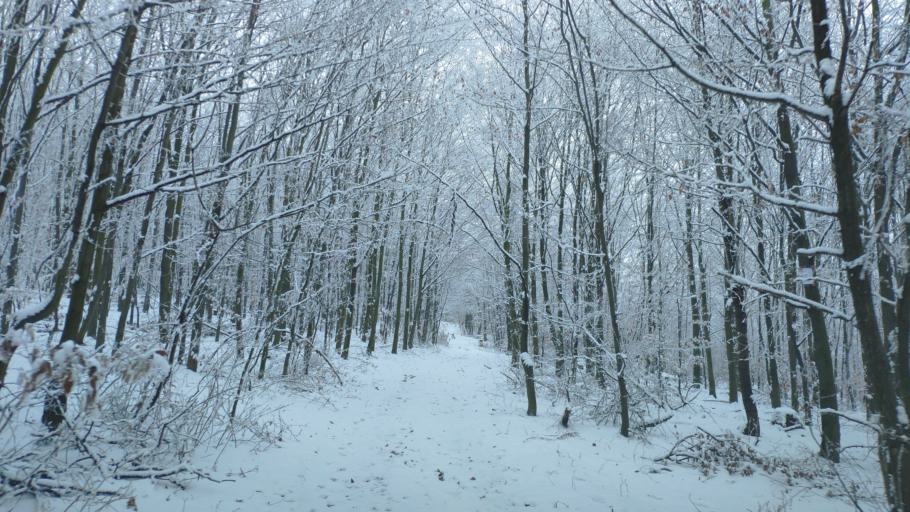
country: SK
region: Kosicky
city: Kosice
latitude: 48.6570
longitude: 21.1816
